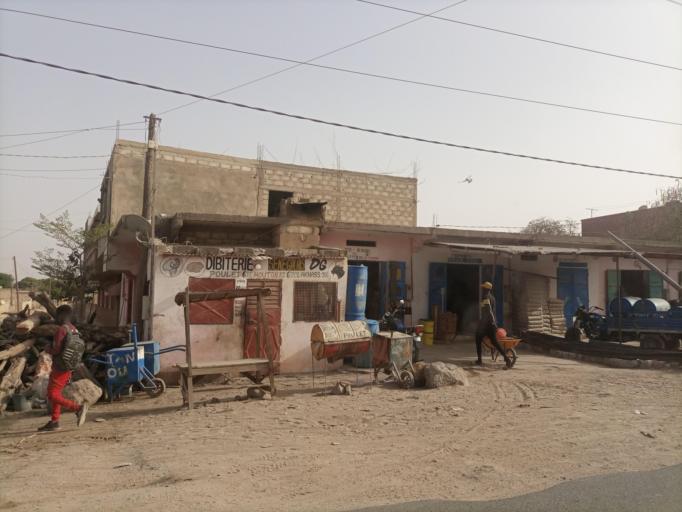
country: SN
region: Thies
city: Nguekhokh
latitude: 14.5831
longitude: -17.0338
